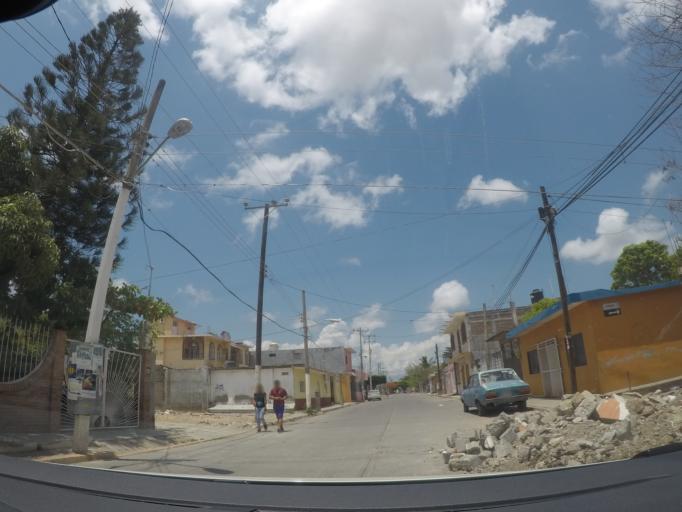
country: MX
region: Oaxaca
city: Juchitan de Zaragoza
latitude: 16.4411
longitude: -95.0124
